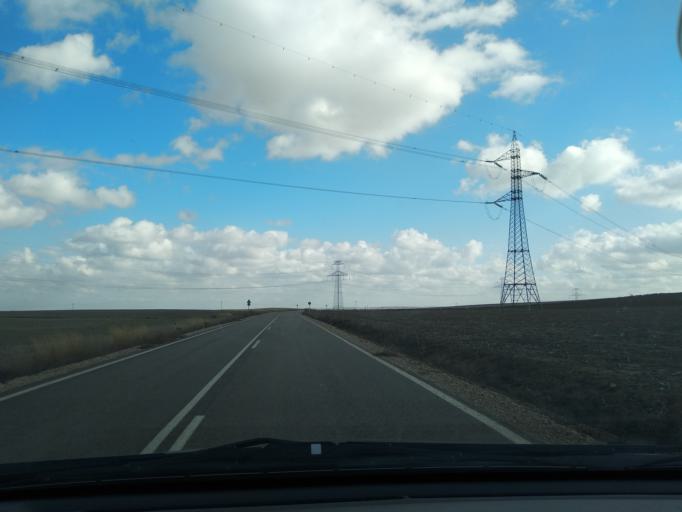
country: ES
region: Castille and Leon
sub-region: Provincia de Valladolid
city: Berrueces
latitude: 41.9491
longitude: -5.0742
